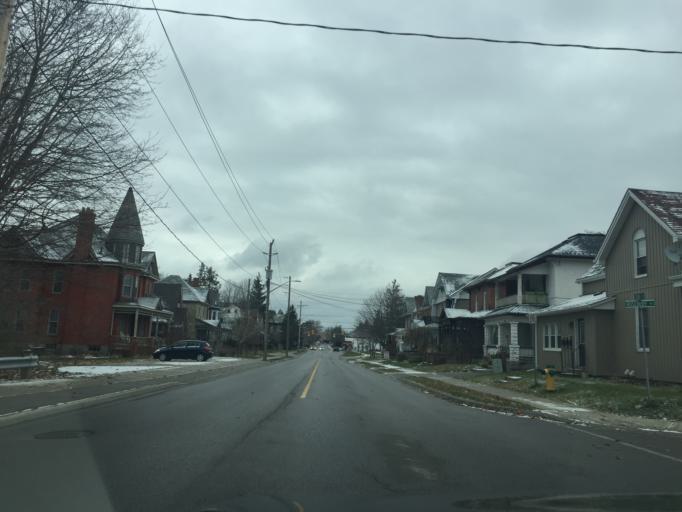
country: CA
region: Ontario
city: St. Thomas
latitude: 42.7736
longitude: -81.1985
